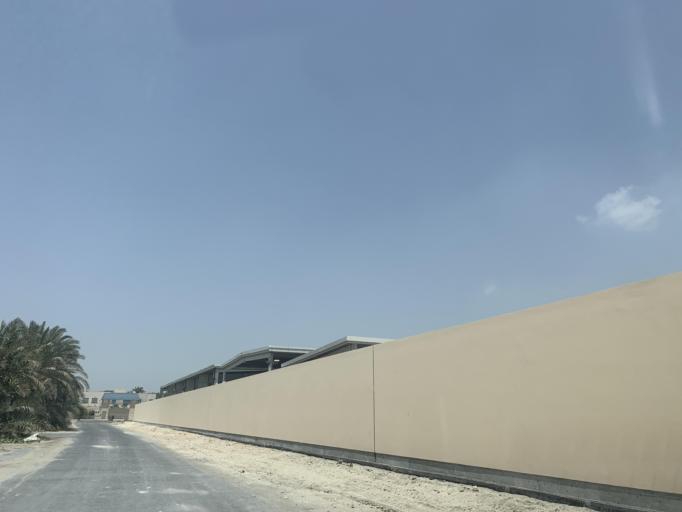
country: BH
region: Central Governorate
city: Madinat Hamad
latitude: 26.1565
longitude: 50.4909
